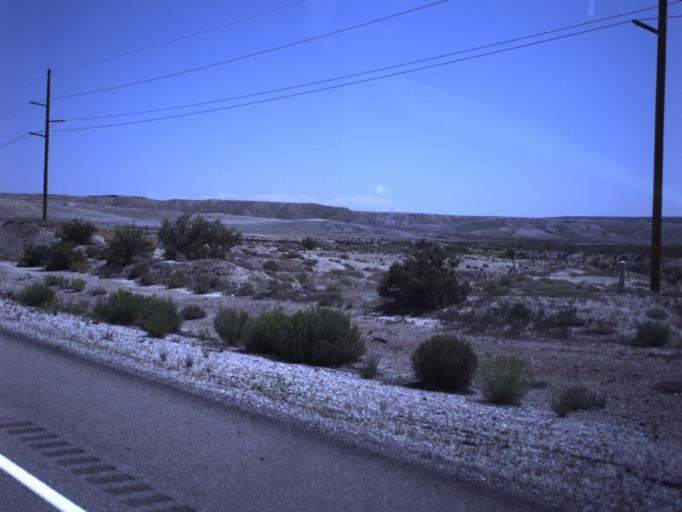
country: US
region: Utah
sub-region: Emery County
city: Ferron
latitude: 38.9373
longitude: -111.2256
